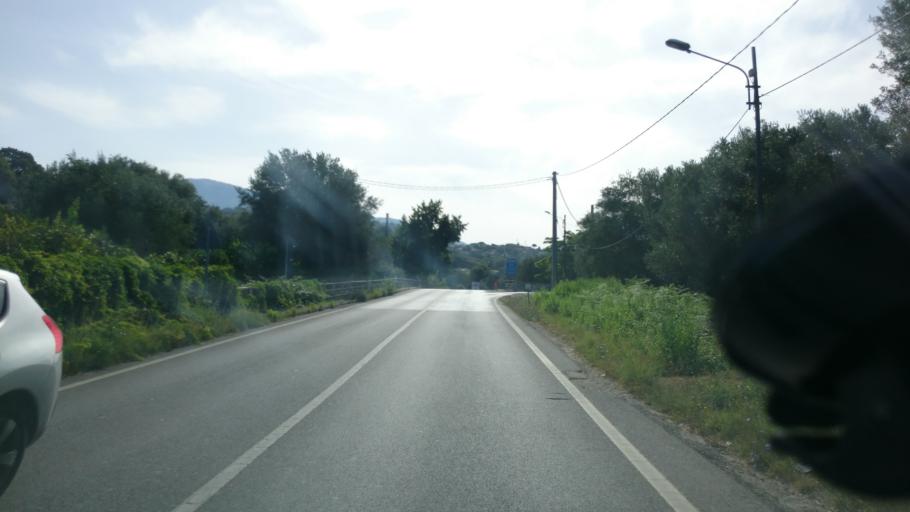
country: IT
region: Campania
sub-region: Provincia di Salerno
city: Villammare
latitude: 40.0807
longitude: 15.5824
